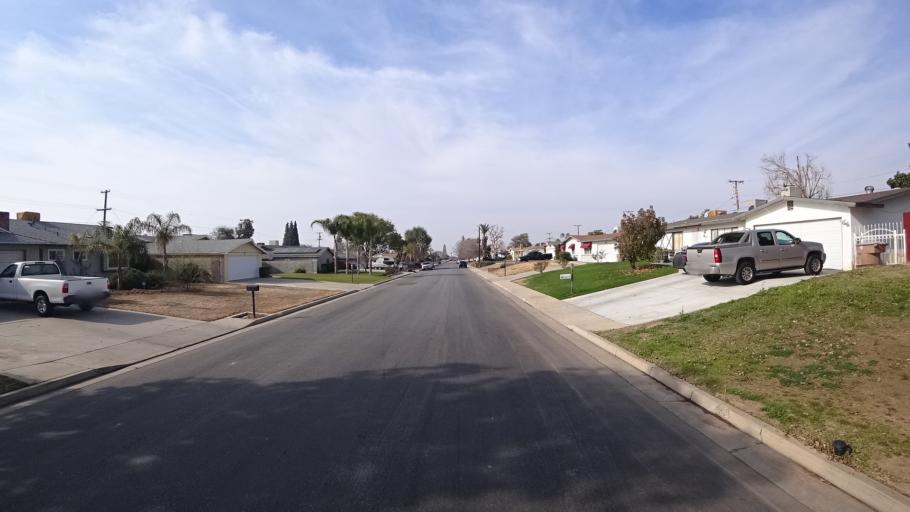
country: US
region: California
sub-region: Kern County
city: Oildale
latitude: 35.4013
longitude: -118.9599
